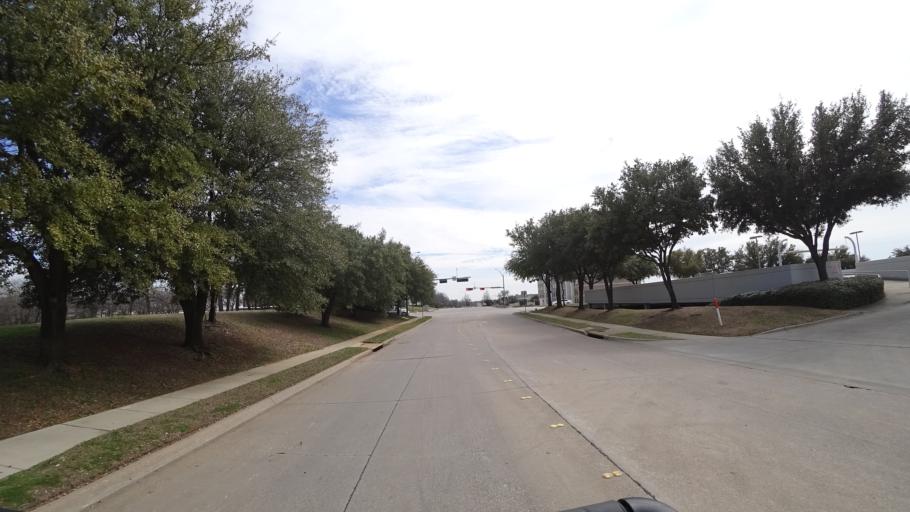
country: US
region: Texas
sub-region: Denton County
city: Lewisville
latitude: 33.0200
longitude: -96.9805
